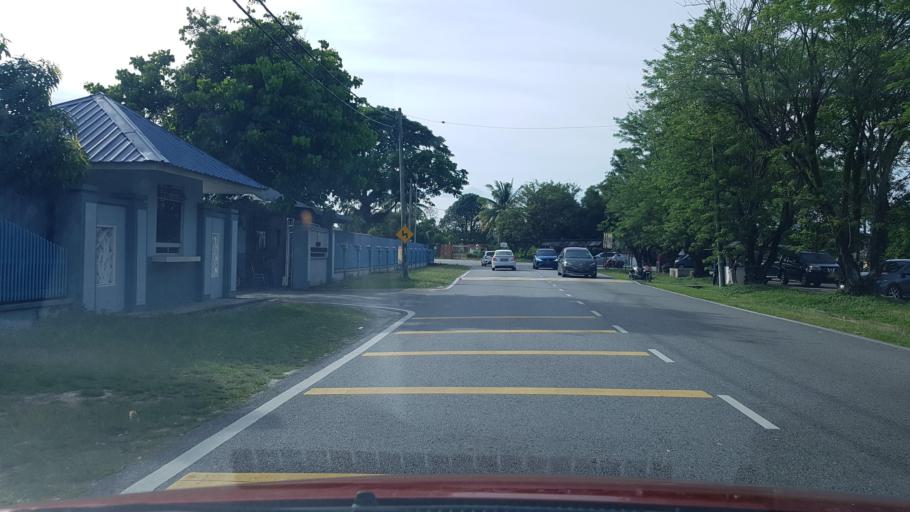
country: MY
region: Terengganu
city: Kuala Terengganu
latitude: 5.3175
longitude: 103.1490
